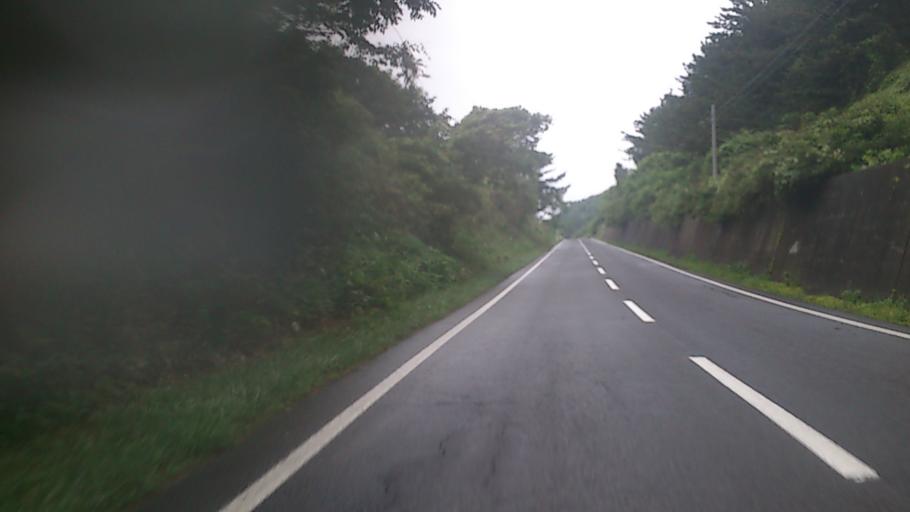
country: JP
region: Akita
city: Noshiromachi
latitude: 40.5168
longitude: 139.9510
